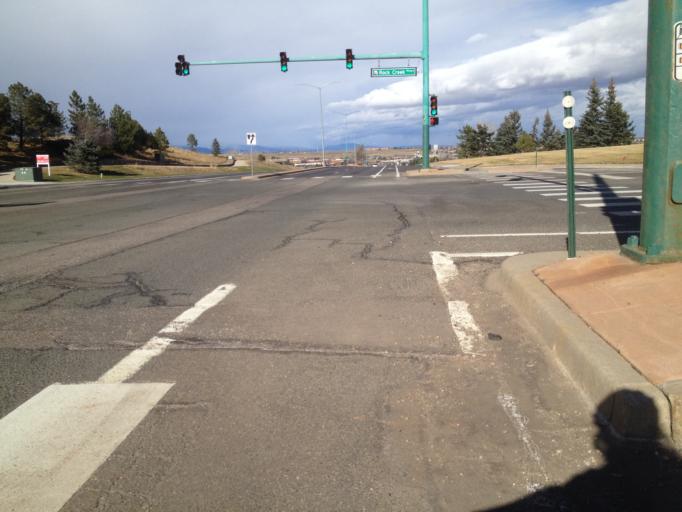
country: US
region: Colorado
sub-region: Boulder County
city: Superior
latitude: 39.9449
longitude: -105.1634
